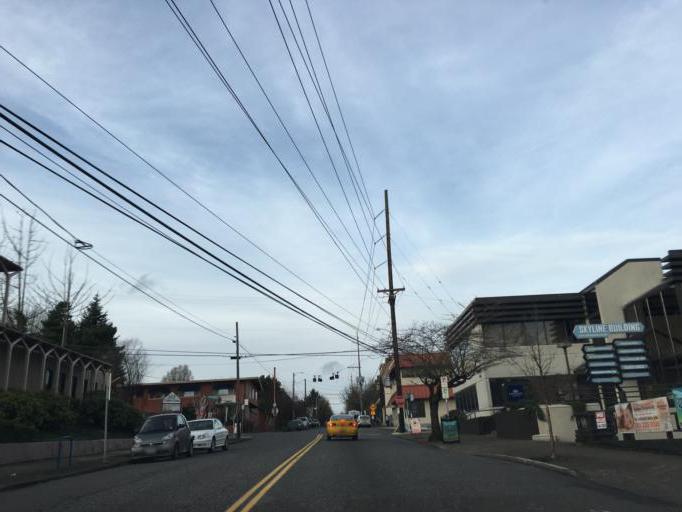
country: US
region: Oregon
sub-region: Multnomah County
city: Portland
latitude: 45.4903
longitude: -122.6762
